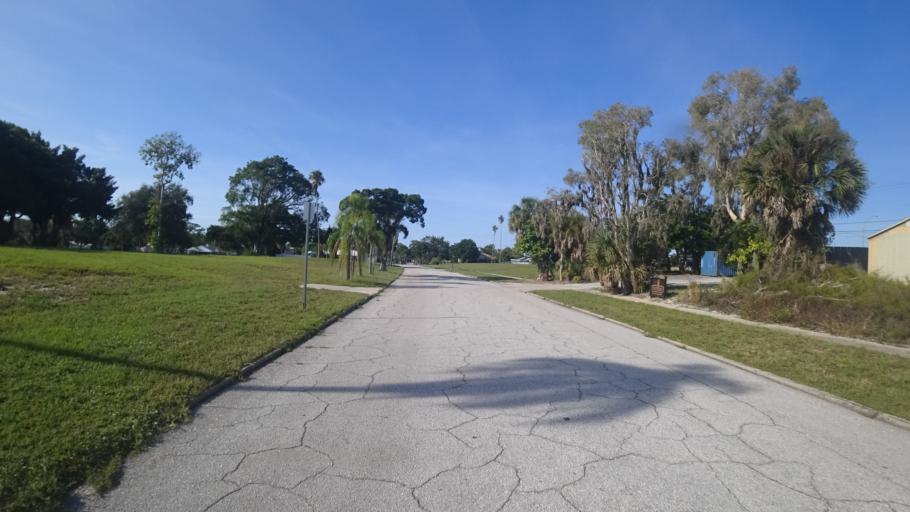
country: US
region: Florida
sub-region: Manatee County
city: Whitfield
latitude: 27.4080
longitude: -82.5710
